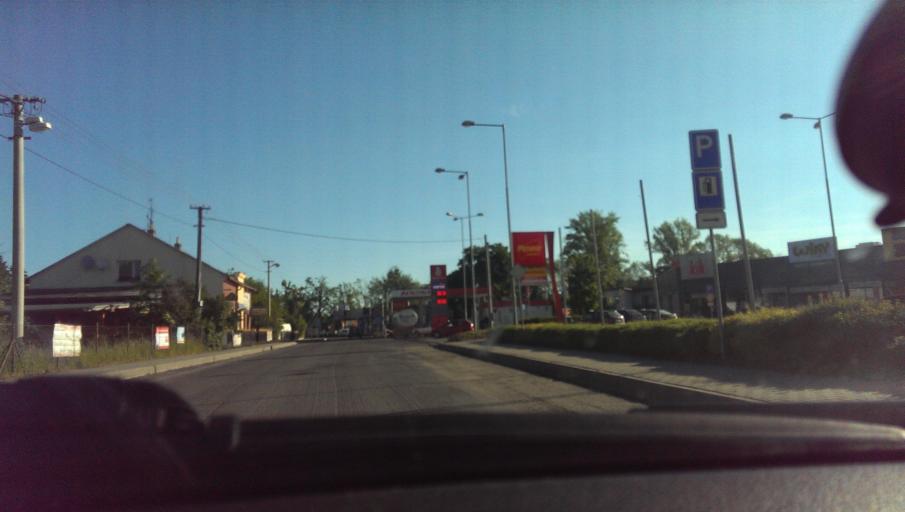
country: CZ
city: Frydlant nad Ostravici
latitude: 49.5837
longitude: 18.3589
